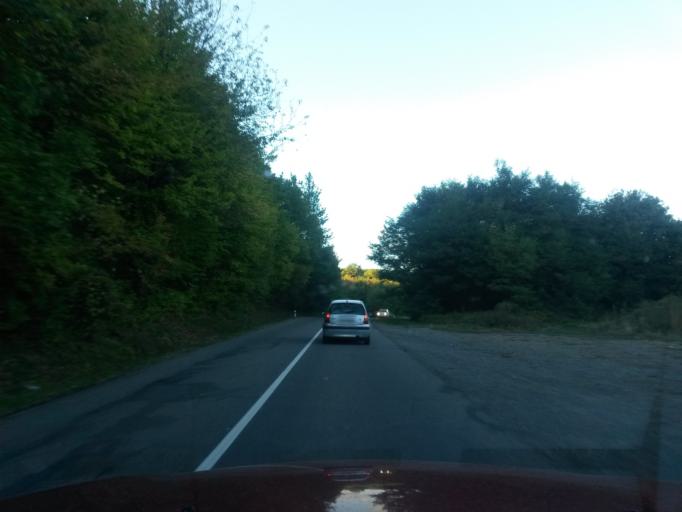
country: SK
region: Kosicky
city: Sobrance
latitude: 48.7868
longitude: 22.2493
